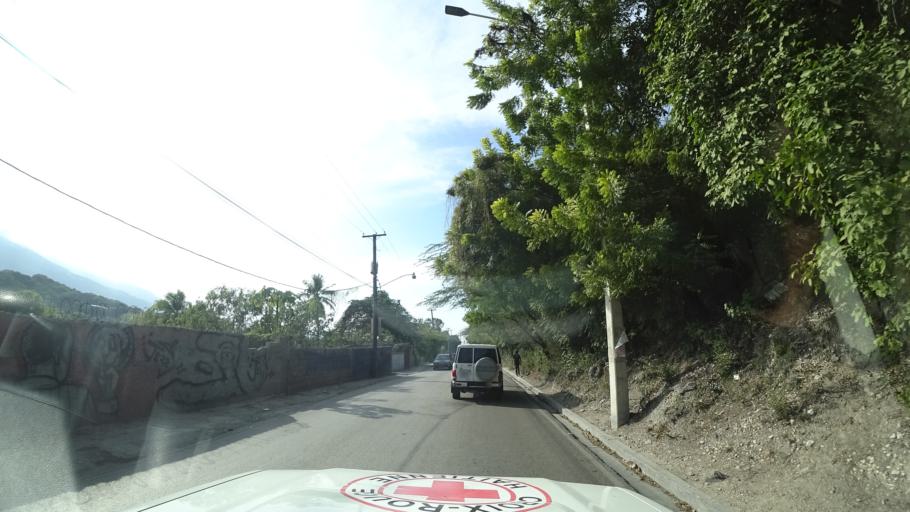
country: HT
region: Ouest
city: Delmas 73
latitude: 18.5333
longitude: -72.3060
